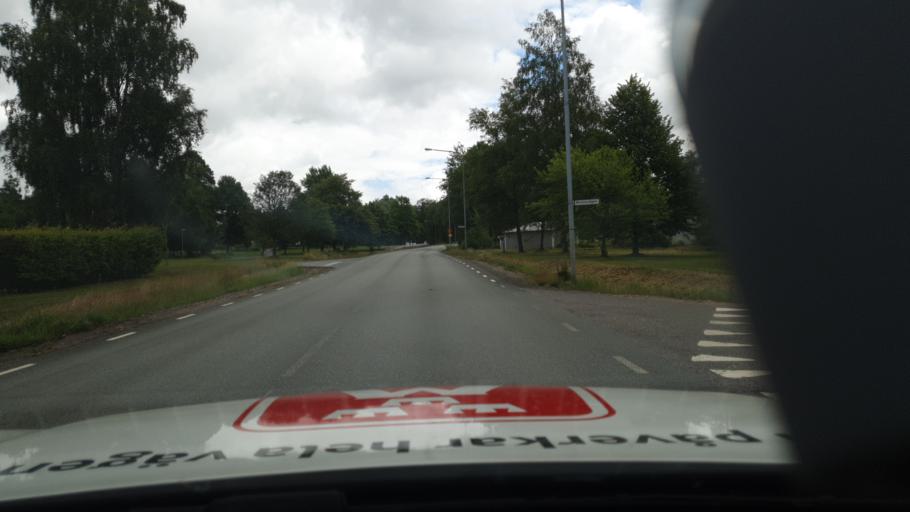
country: SE
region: Joenkoeping
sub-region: Mullsjo Kommun
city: Mullsjoe
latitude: 57.9201
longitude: 13.8723
